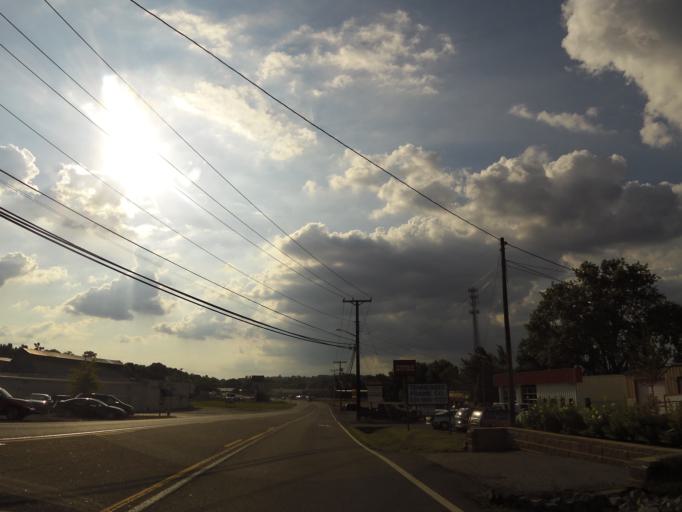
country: US
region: Tennessee
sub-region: Montgomery County
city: Clarksville
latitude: 36.5399
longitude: -87.3413
